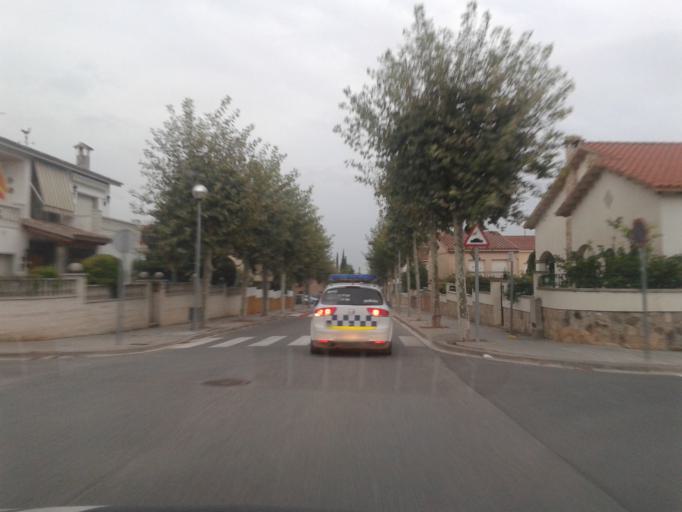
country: ES
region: Catalonia
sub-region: Provincia de Barcelona
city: Castellet
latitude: 41.2666
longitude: 1.5988
